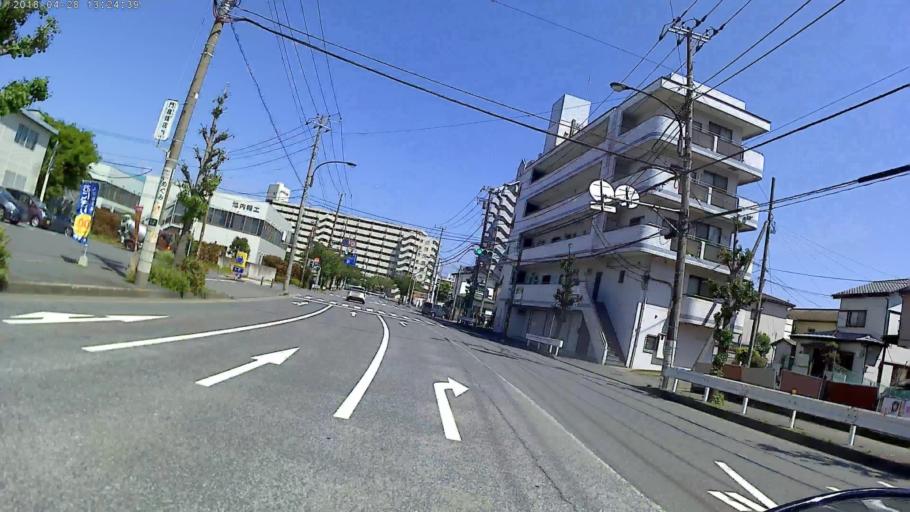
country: JP
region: Kanagawa
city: Yokosuka
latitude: 35.2321
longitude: 139.6966
